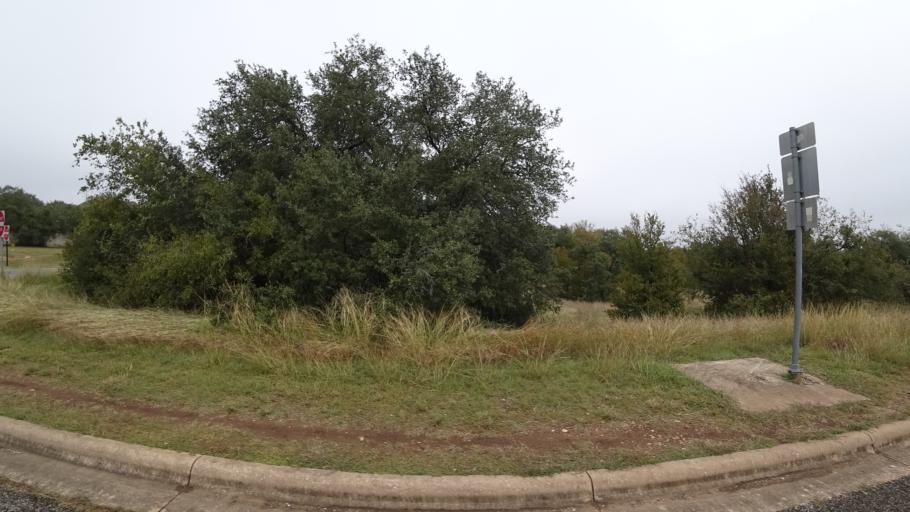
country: US
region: Texas
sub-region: Travis County
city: Shady Hollow
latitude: 30.1910
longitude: -97.8741
